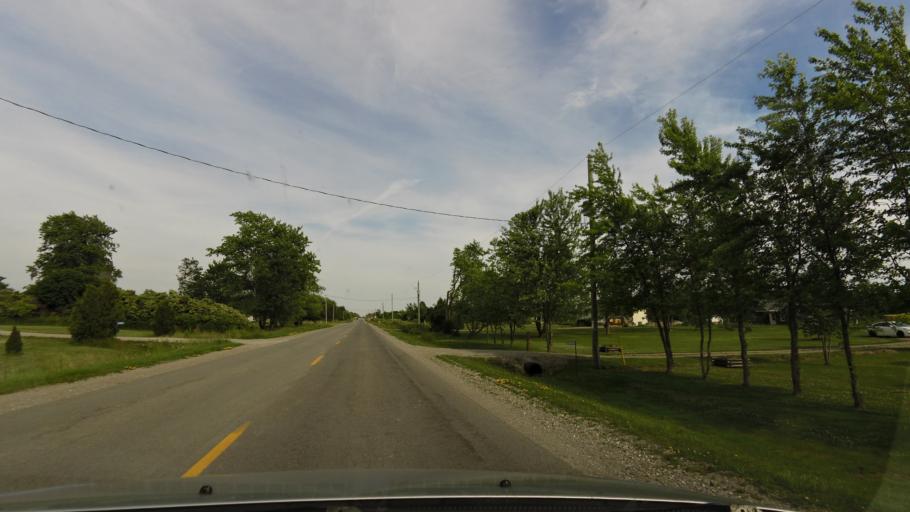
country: CA
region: Ontario
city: Ancaster
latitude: 43.0350
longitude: -80.0262
